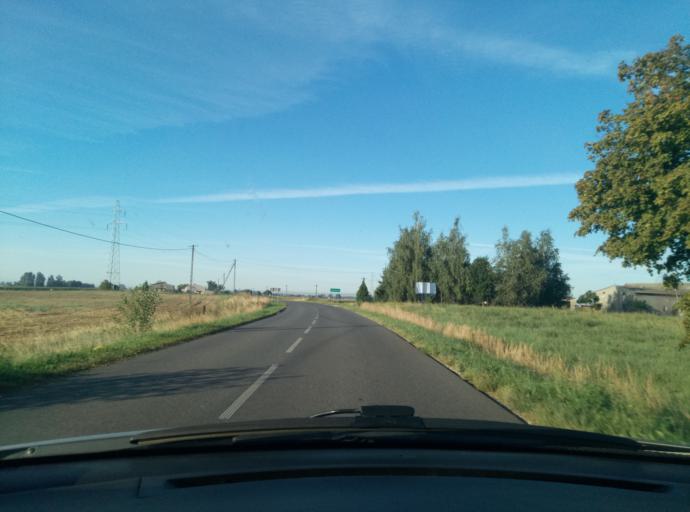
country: PL
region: Kujawsko-Pomorskie
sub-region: Powiat golubsko-dobrzynski
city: Kowalewo Pomorskie
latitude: 53.1824
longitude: 18.9036
